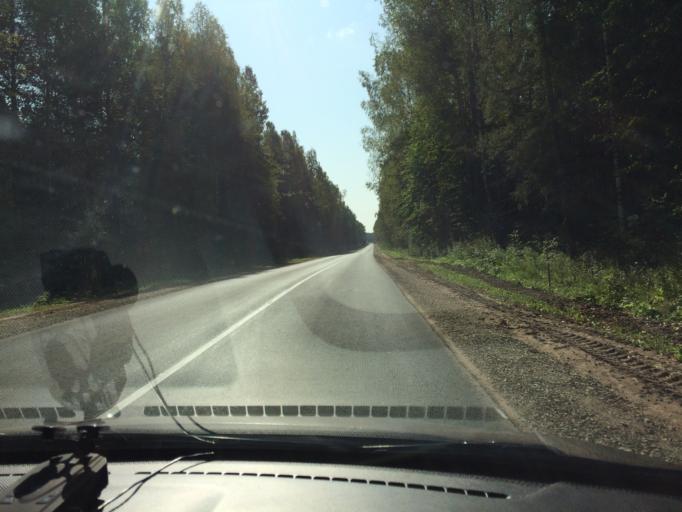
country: RU
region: Mariy-El
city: Surok
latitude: 56.5628
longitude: 48.3036
